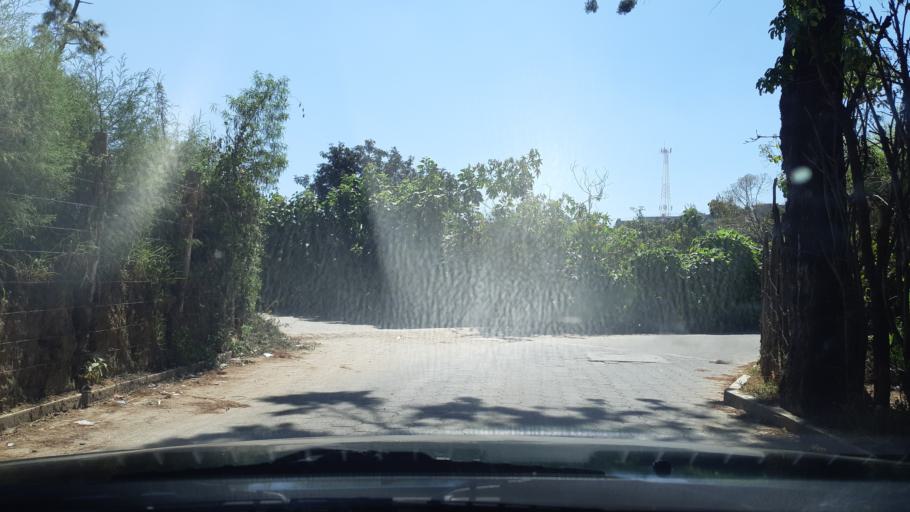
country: GT
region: Chimaltenango
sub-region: Municipio de Chimaltenango
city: Chimaltenango
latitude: 14.6698
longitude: -90.8422
